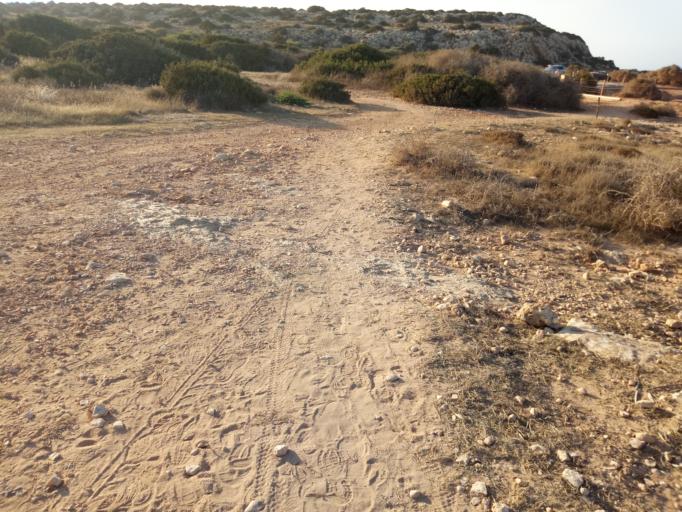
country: CY
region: Ammochostos
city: Protaras
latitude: 34.9712
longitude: 34.0752
